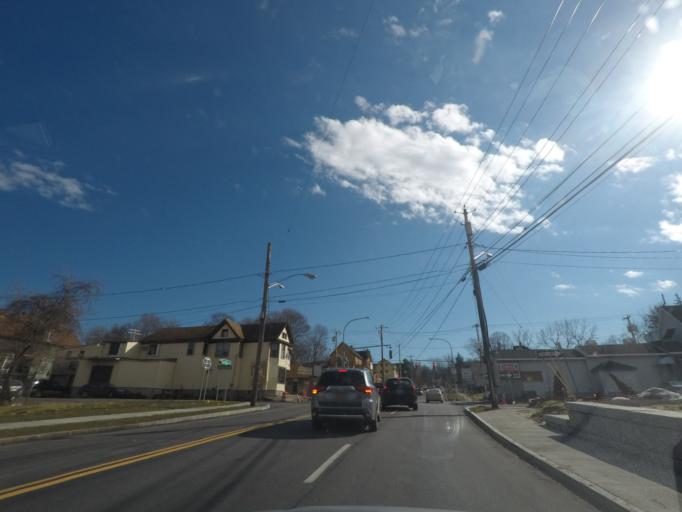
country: US
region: New York
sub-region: Onondaga County
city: Syracuse
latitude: 43.0488
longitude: -76.1214
